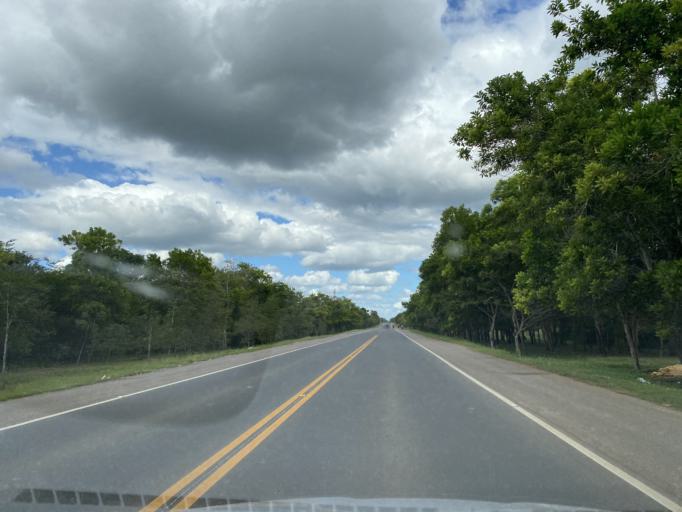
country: DO
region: Santo Domingo
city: Guerra
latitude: 18.6138
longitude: -69.7674
